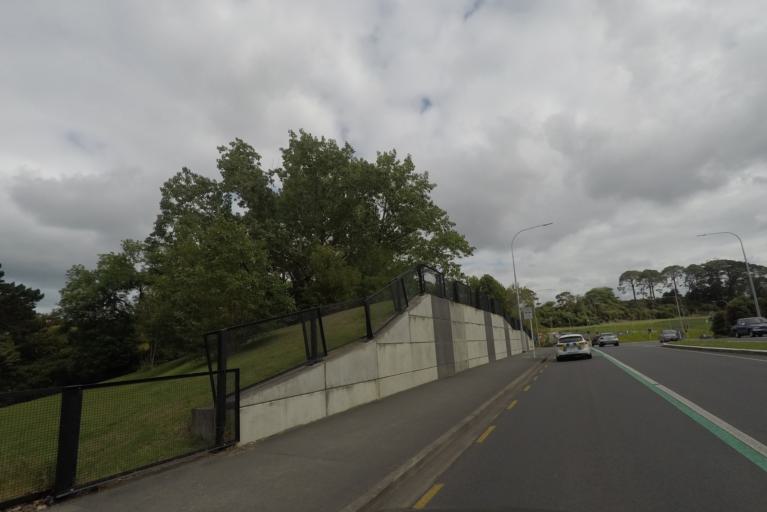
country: NZ
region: Auckland
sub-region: Auckland
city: Rothesay Bay
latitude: -36.7291
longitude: 174.6972
